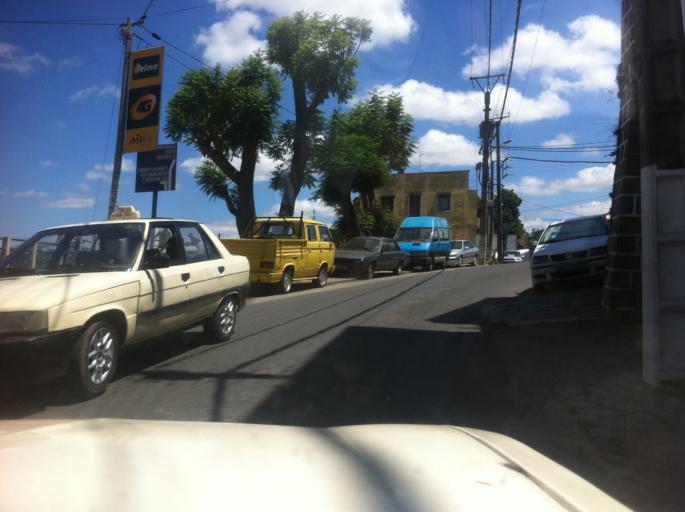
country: MG
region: Analamanga
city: Antananarivo
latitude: -18.9118
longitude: 47.5256
